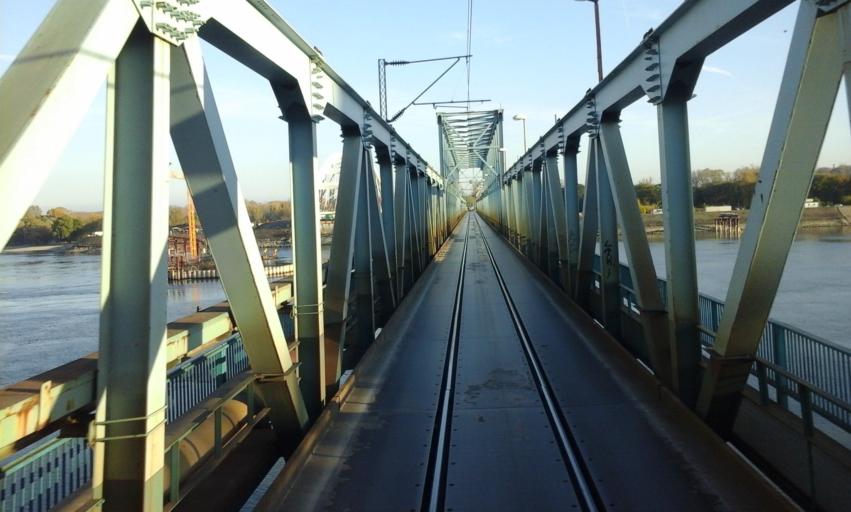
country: RS
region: Autonomna Pokrajina Vojvodina
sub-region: Juznobacki Okrug
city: Novi Sad
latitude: 45.2628
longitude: 19.8576
